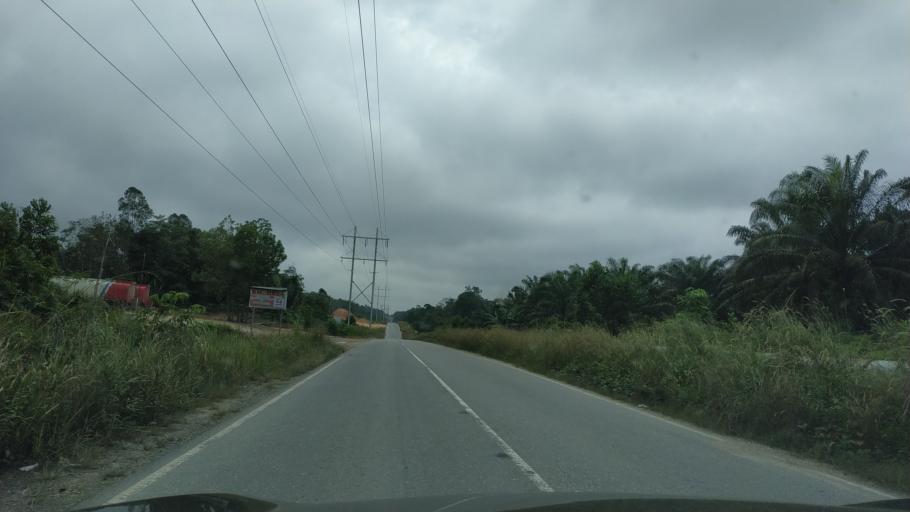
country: ID
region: Riau
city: Pekanbaru
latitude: 0.6435
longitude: 101.6774
